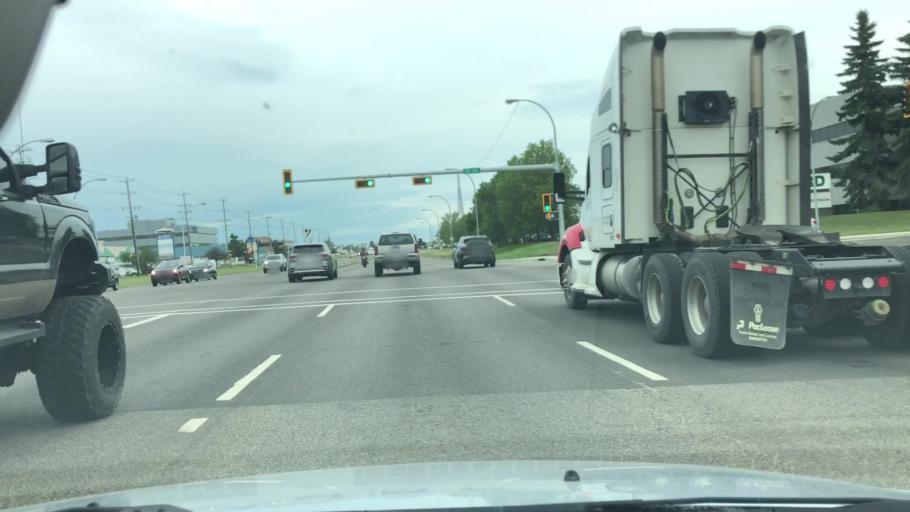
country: CA
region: Alberta
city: St. Albert
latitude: 53.5536
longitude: -113.6154
